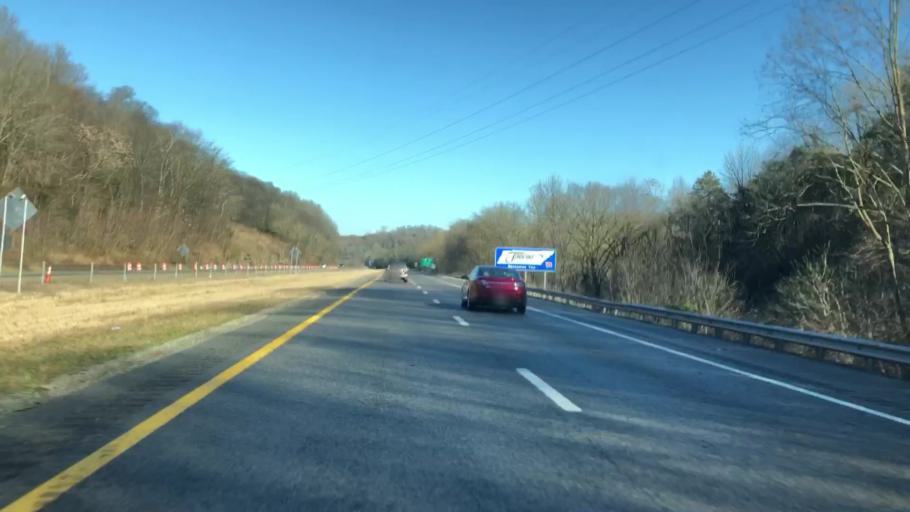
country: US
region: Alabama
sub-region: Limestone County
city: Ardmore
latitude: 34.9934
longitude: -86.8787
